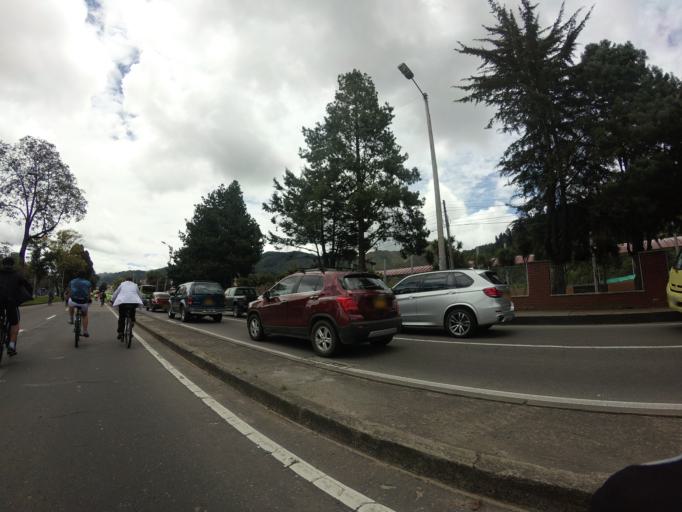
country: CO
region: Bogota D.C.
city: Barrio San Luis
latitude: 4.6825
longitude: -74.0368
